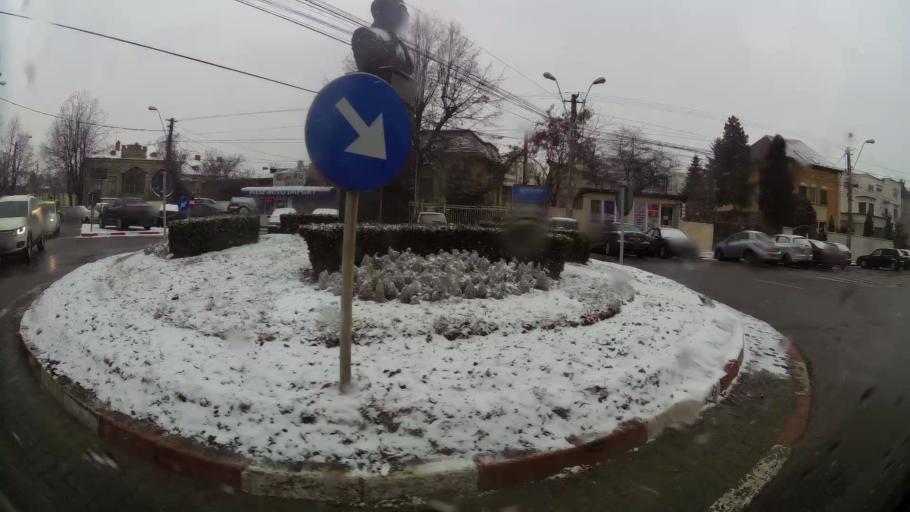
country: RO
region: Prahova
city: Ploiesti
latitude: 44.9389
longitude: 26.0209
